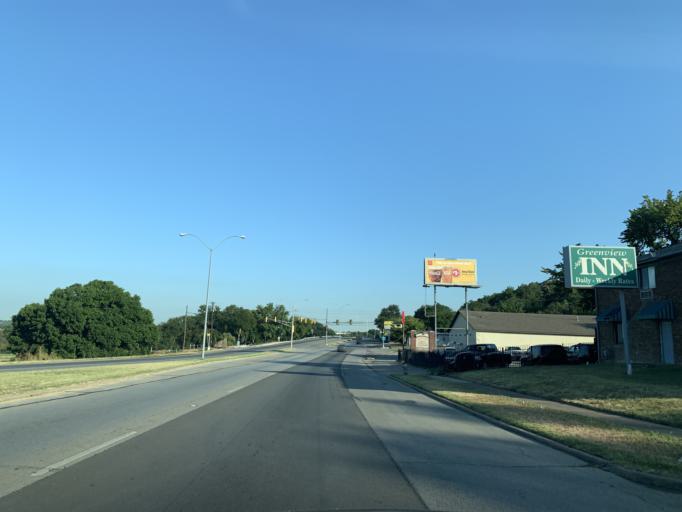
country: US
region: Texas
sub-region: Tarrant County
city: River Oaks
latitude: 32.7748
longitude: -97.3665
